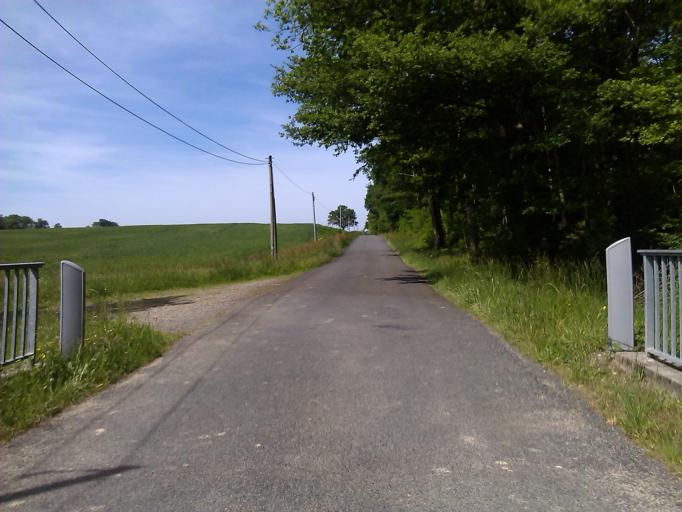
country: FR
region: Auvergne
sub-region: Departement de l'Allier
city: Lusigny
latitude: 46.5676
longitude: 3.4461
